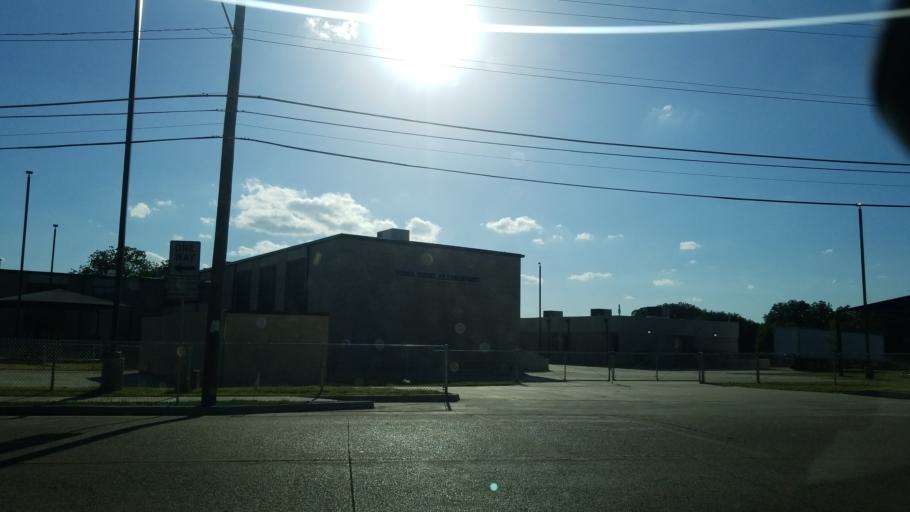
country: US
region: Texas
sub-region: Dallas County
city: Highland Park
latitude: 32.7851
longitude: -96.7058
